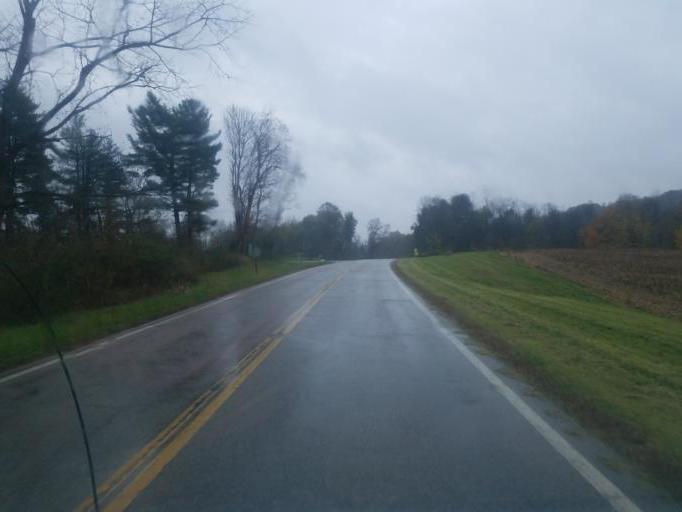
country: US
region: Ohio
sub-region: Morgan County
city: McConnelsville
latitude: 39.6147
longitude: -81.8266
